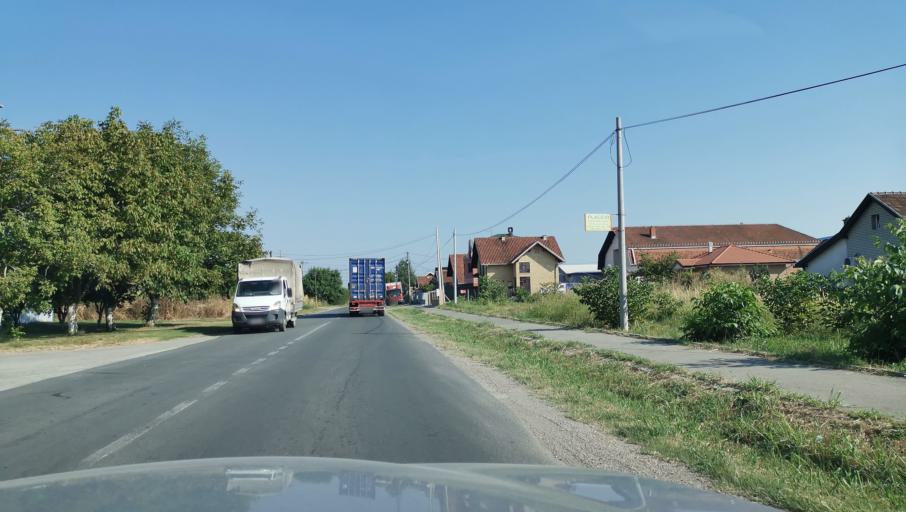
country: RS
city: Dobanovci
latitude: 44.8151
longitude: 20.2368
